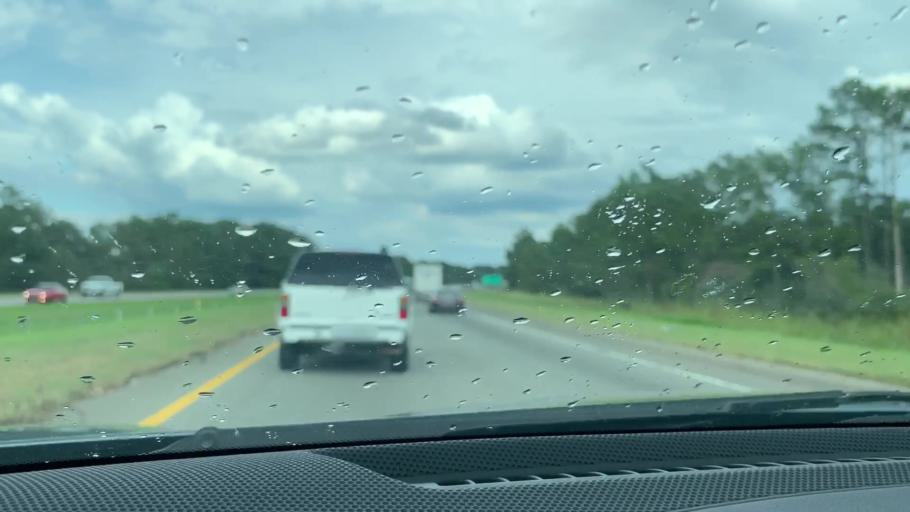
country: US
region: South Carolina
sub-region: Hampton County
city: Yemassee
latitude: 32.5908
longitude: -80.9212
